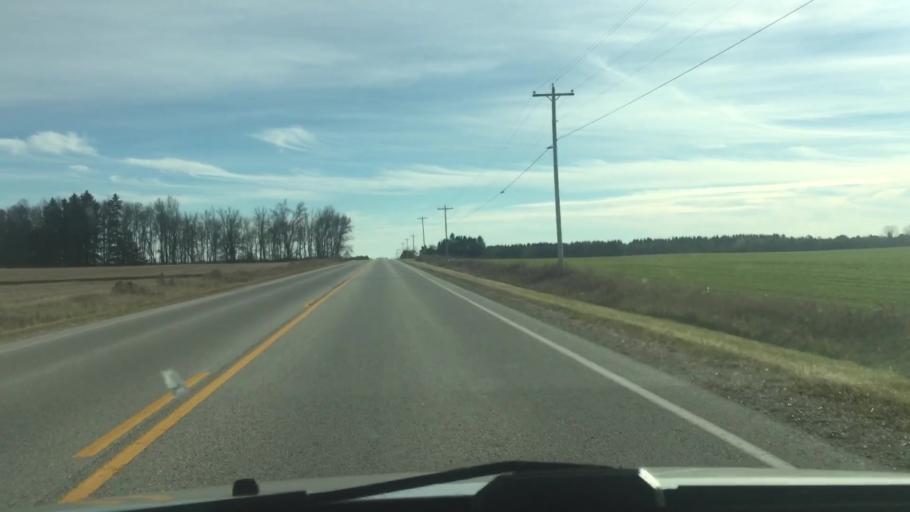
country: US
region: Wisconsin
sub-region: Kewaunee County
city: Algoma
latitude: 44.6605
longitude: -87.3977
